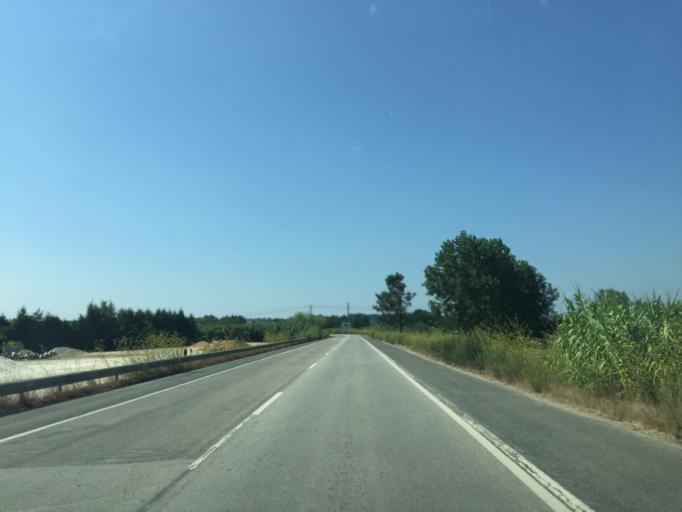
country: PT
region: Aveiro
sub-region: Mealhada
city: Mealhada
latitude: 40.3714
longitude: -8.4694
